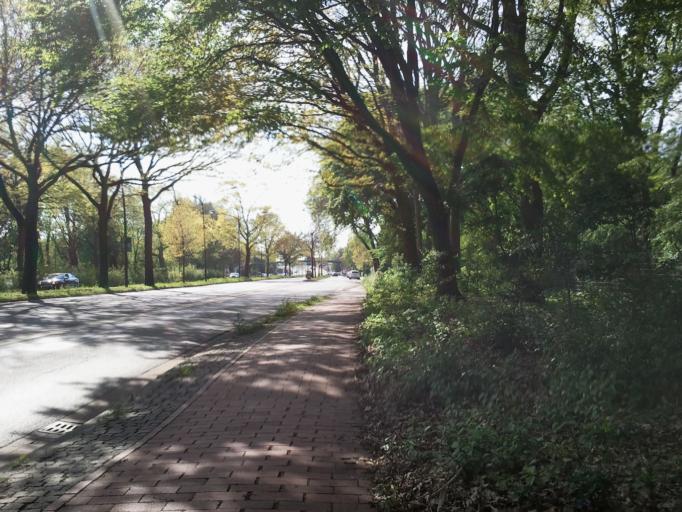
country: DE
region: Bremen
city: Bremen
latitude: 53.0825
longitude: 8.8636
